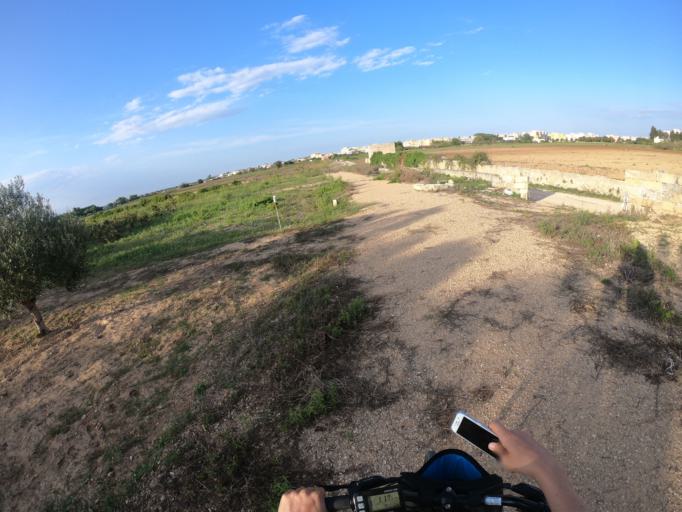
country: IT
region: Apulia
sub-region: Provincia di Lecce
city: Nardo
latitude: 40.1640
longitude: 18.0167
